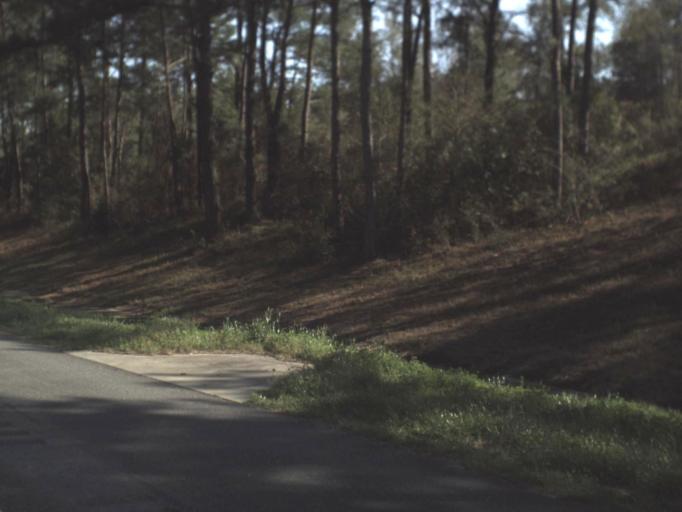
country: US
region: Florida
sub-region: Gadsden County
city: Midway
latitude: 30.5212
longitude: -84.4907
